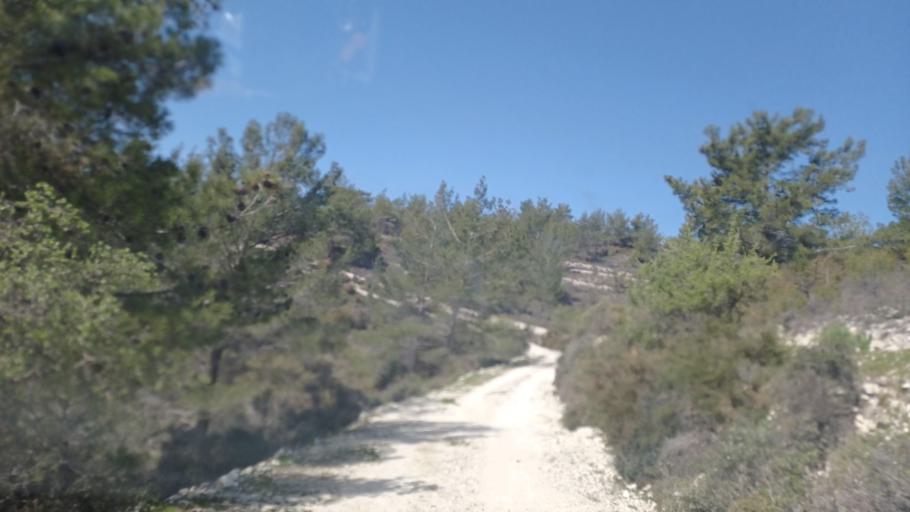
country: CY
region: Limassol
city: Pachna
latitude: 34.8861
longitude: 32.7230
